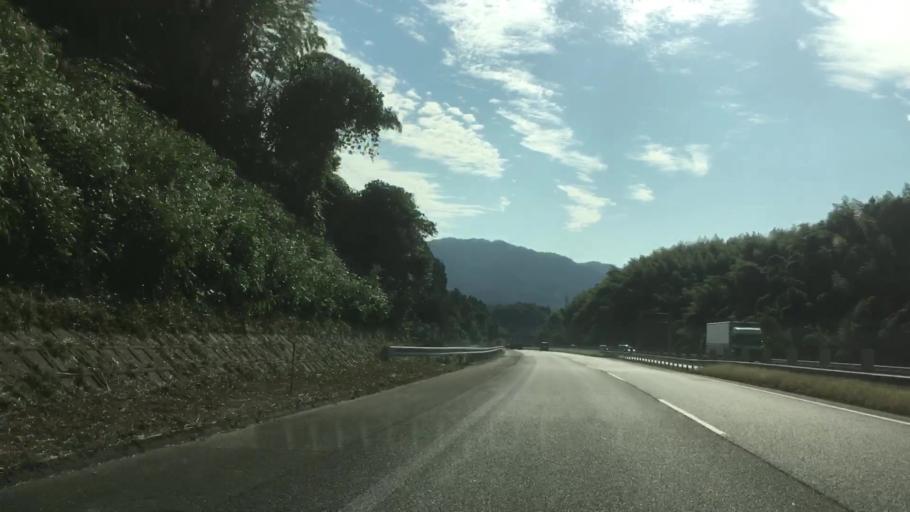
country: JP
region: Yamaguchi
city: Hikari
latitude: 34.0331
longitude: 131.9684
